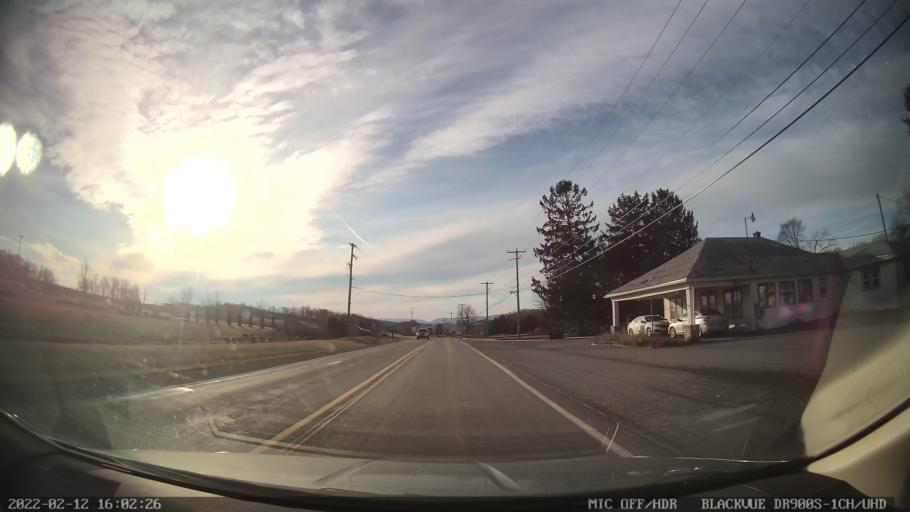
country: US
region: Pennsylvania
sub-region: Berks County
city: Kutztown
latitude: 40.5808
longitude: -75.7744
